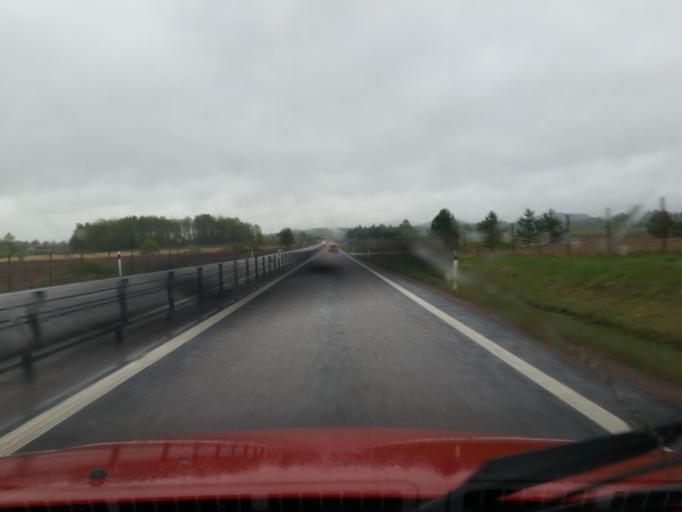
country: SE
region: Dalarna
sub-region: Borlange Kommun
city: Ornas
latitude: 60.4223
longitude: 15.5441
